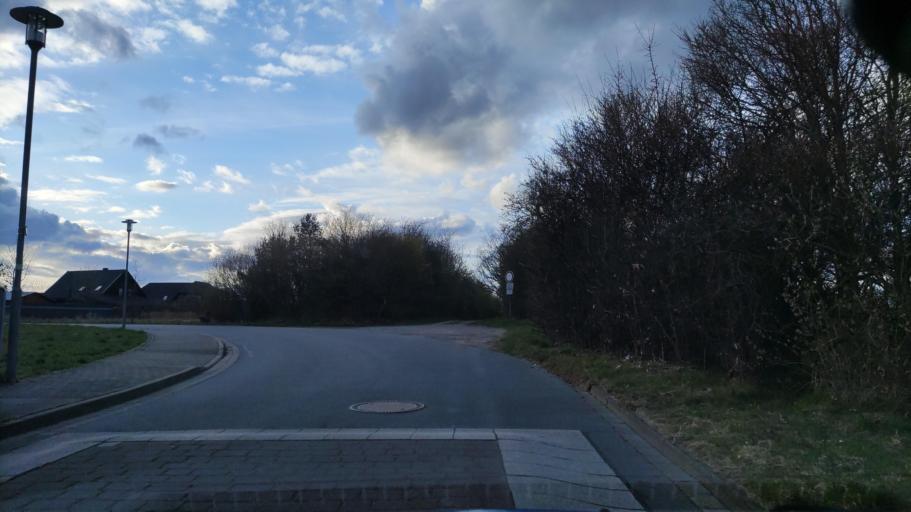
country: DE
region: Lower Saxony
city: Bad Bevensen
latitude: 53.0941
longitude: 10.5582
